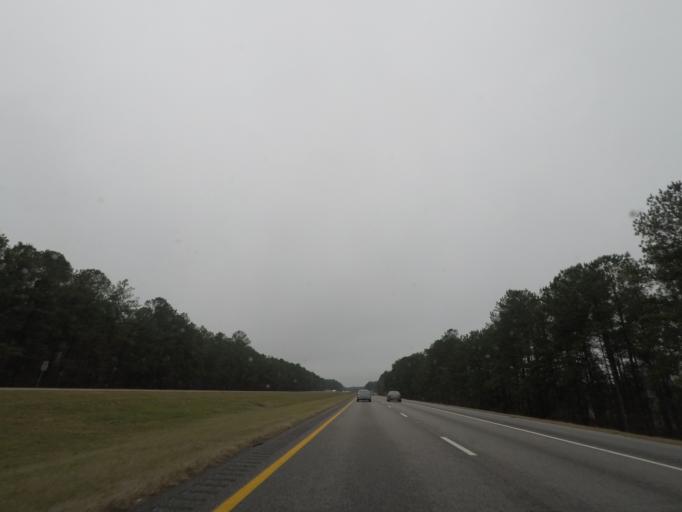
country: US
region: South Carolina
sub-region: Sumter County
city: East Sumter
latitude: 33.9086
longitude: -80.0891
